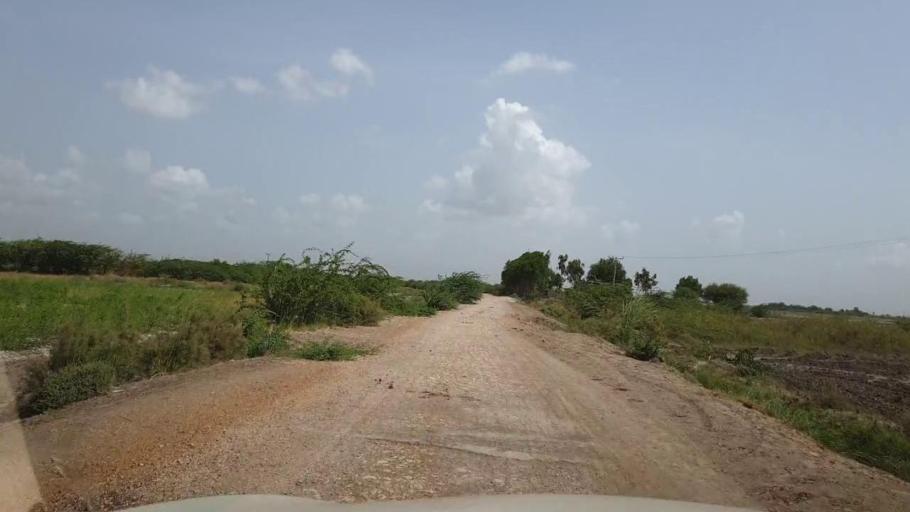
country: PK
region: Sindh
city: Kadhan
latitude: 24.4020
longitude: 68.7988
